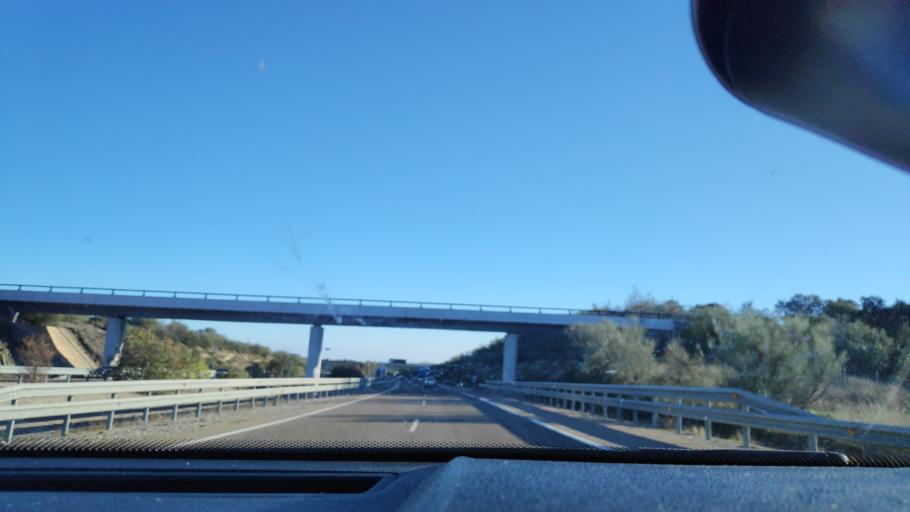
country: ES
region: Andalusia
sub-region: Provincia de Sevilla
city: Gerena
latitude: 37.5839
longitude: -6.1208
